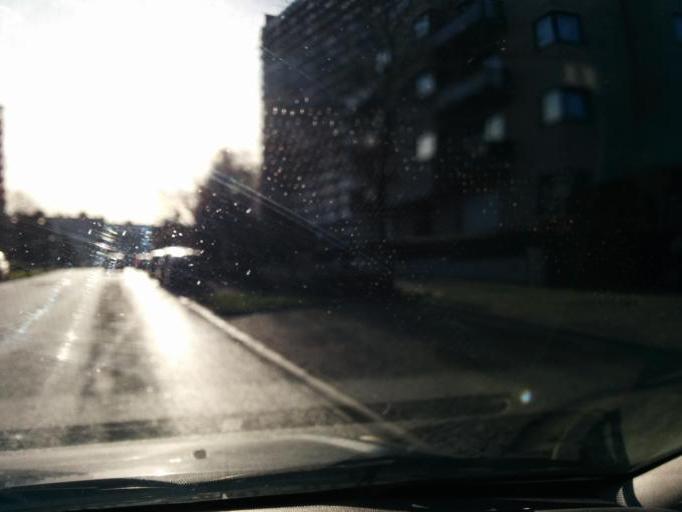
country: BE
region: Flanders
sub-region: Provincie Vlaams-Brabant
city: Wemmel
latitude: 50.8746
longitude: 4.2999
